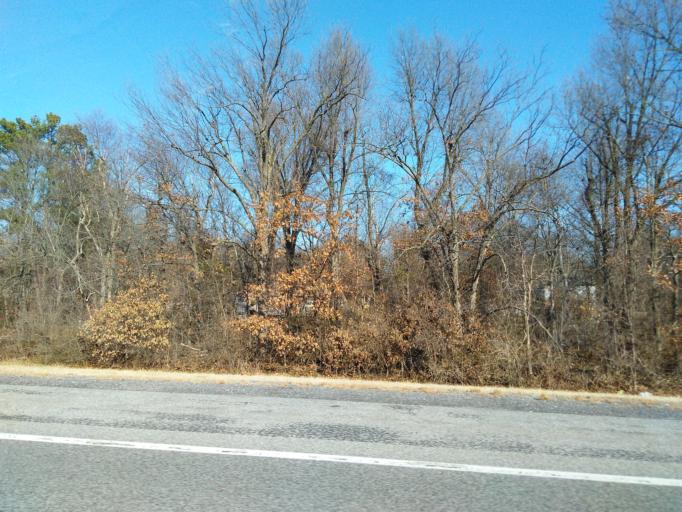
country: US
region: Kentucky
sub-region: McCracken County
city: Hendron
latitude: 37.0559
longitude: -88.6528
